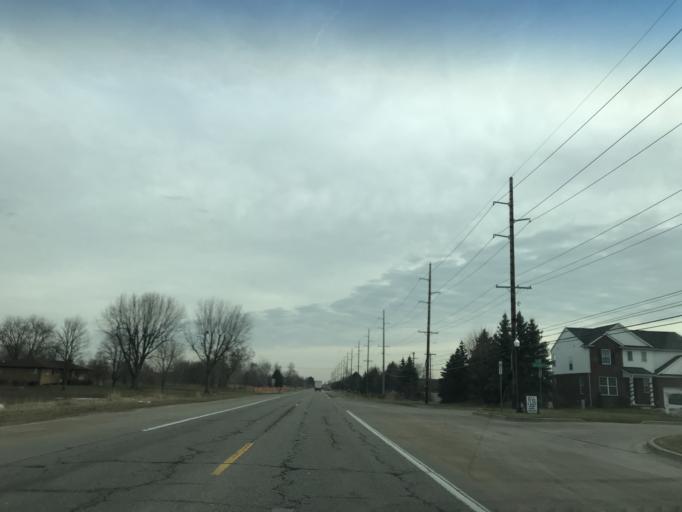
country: US
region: Michigan
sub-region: Macomb County
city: Mount Clemens
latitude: 42.6727
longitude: -82.9142
